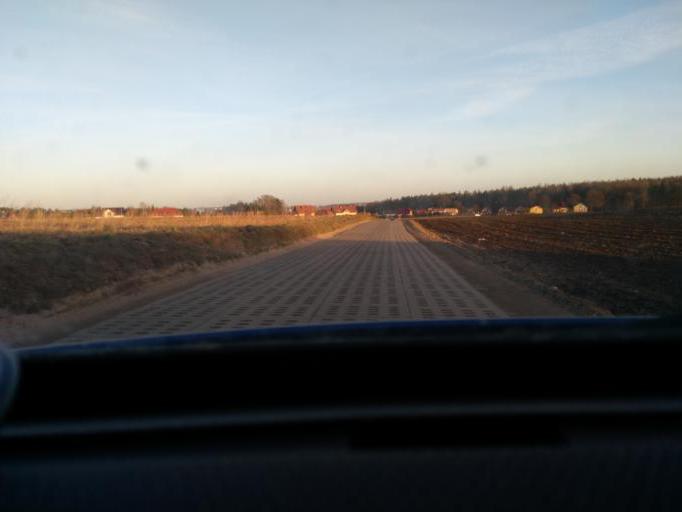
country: PL
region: Pomeranian Voivodeship
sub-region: Powiat kartuski
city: Banino
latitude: 54.3804
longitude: 18.4011
